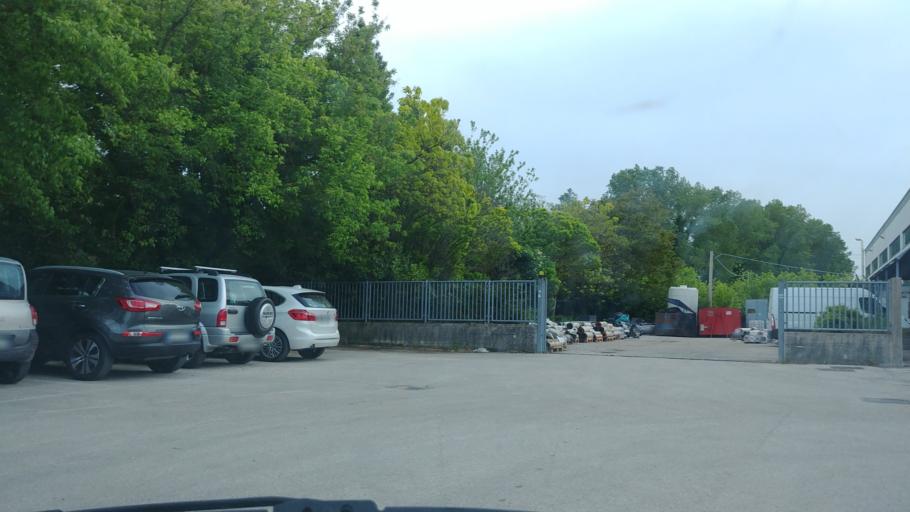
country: IT
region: The Marches
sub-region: Provincia di Pesaro e Urbino
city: Villa Ceccolini
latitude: 43.8951
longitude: 12.8437
